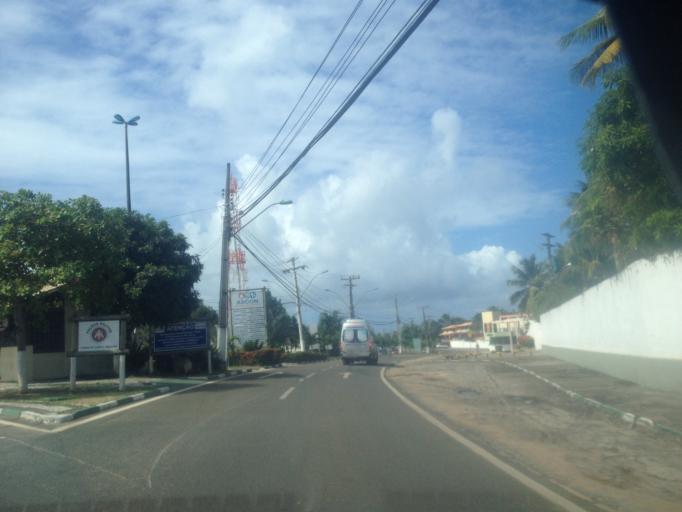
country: BR
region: Bahia
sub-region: Mata De Sao Joao
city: Mata de Sao Joao
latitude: -12.6475
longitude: -38.0789
